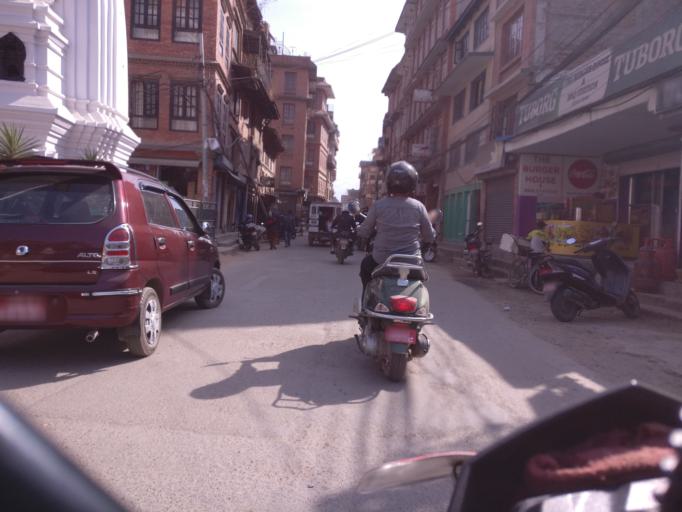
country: NP
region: Central Region
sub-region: Bagmati Zone
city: Patan
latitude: 27.6707
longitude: 85.3268
